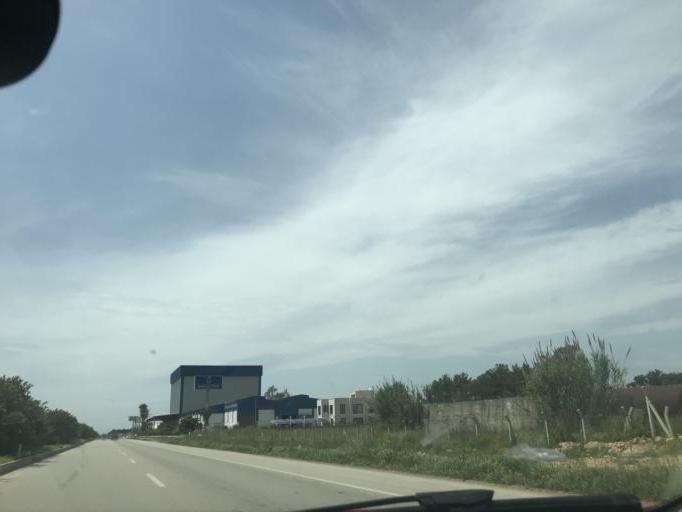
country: TR
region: Adana
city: Yakapinar
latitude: 36.9699
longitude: 35.5334
